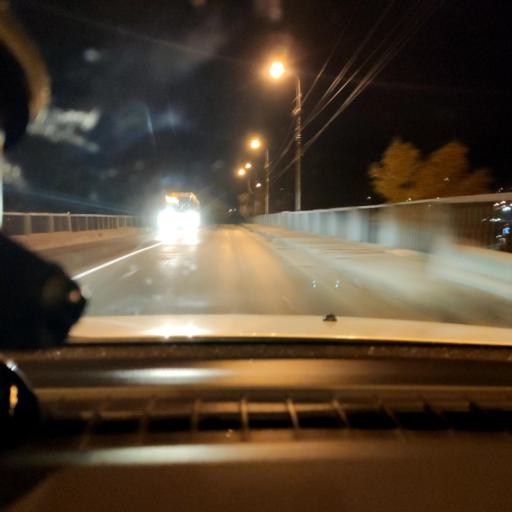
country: RU
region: Samara
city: Rozhdestveno
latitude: 53.1512
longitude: 50.0673
